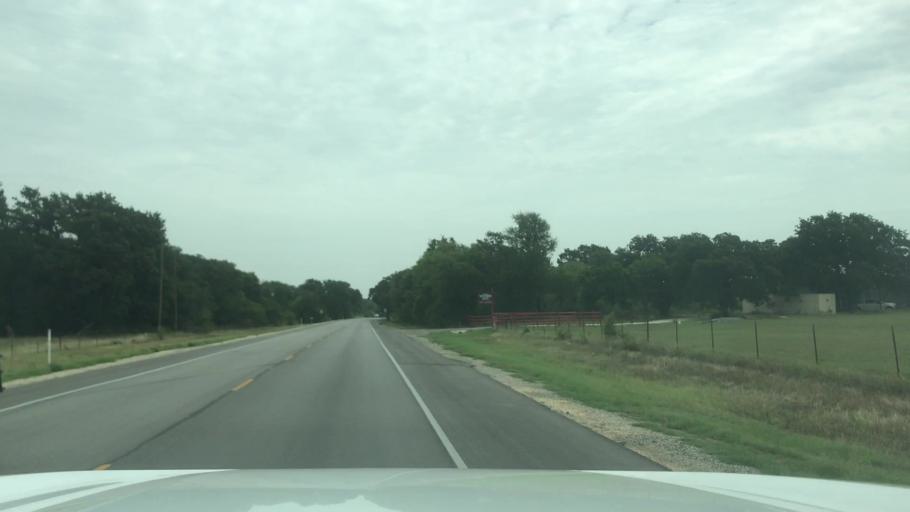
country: US
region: Texas
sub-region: Erath County
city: Dublin
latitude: 32.0875
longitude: -98.3061
